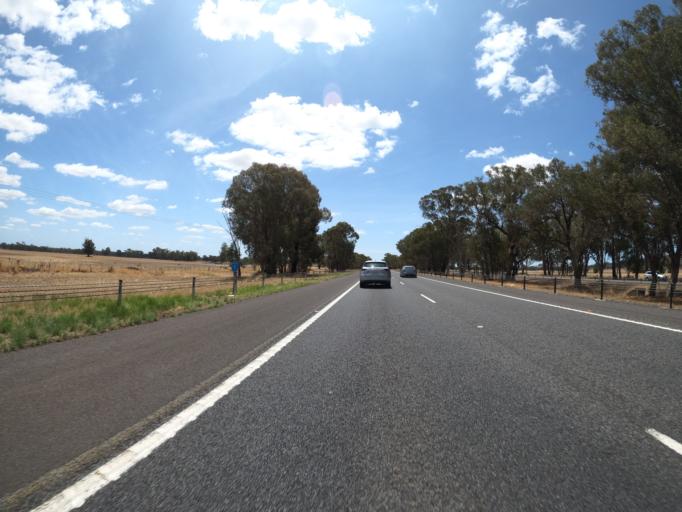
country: AU
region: Victoria
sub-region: Benalla
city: Benalla
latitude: -36.6628
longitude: 145.6869
